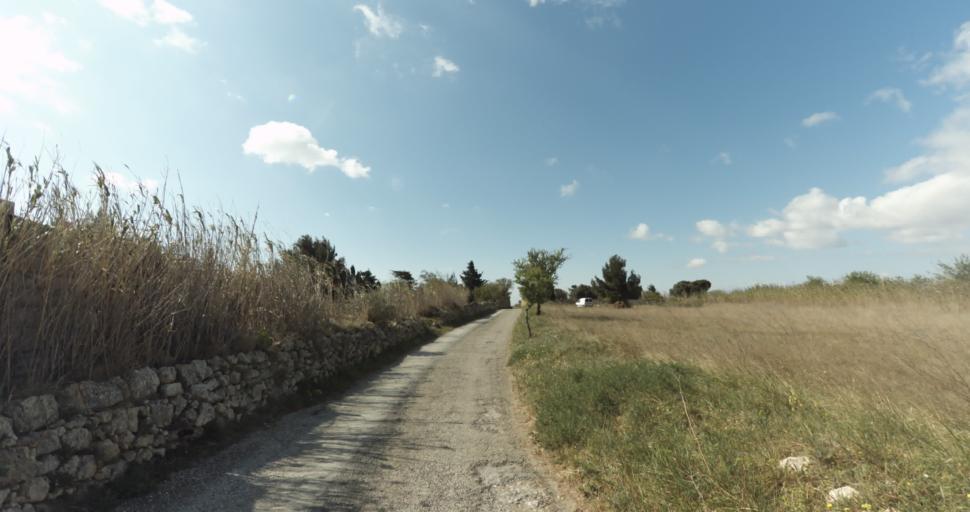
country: FR
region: Languedoc-Roussillon
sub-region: Departement de l'Aude
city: Leucate
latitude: 42.9258
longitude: 3.0376
